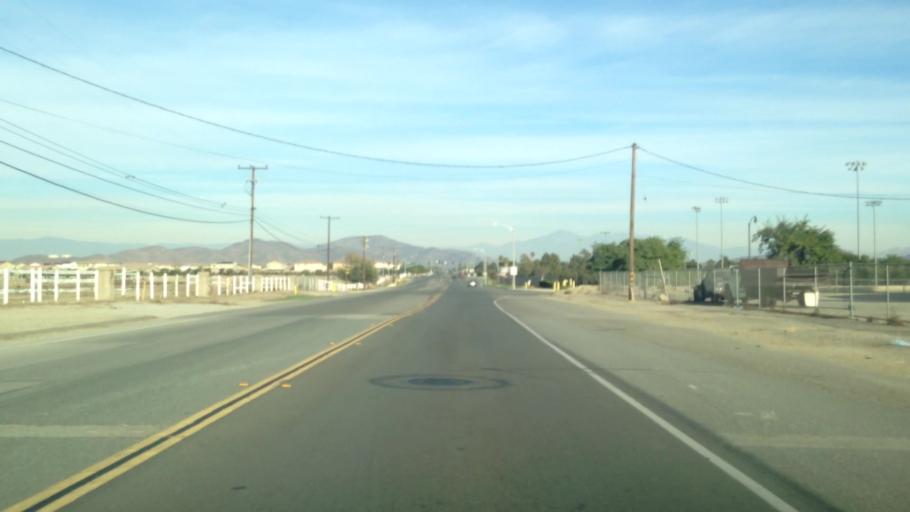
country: US
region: California
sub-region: Riverside County
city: Mira Loma
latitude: 33.9924
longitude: -117.5459
